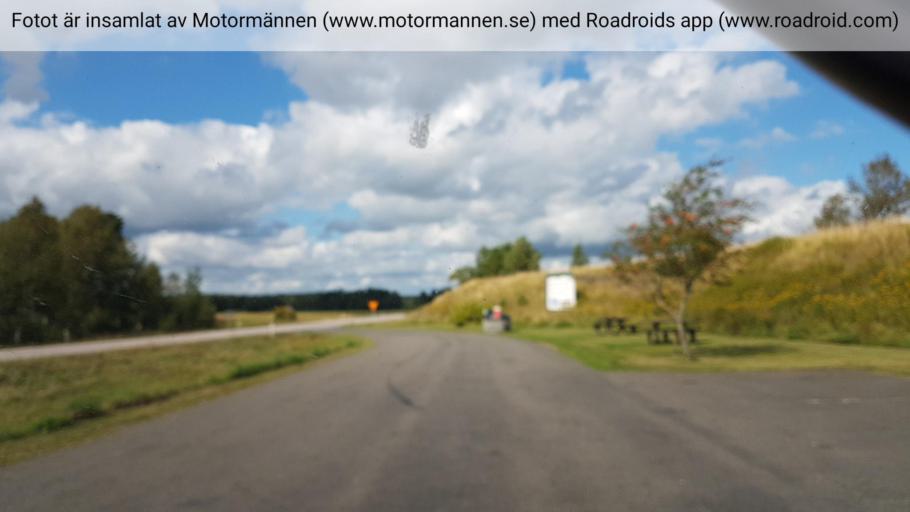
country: SE
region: Vaestra Goetaland
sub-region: Falkopings Kommun
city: Falkoeping
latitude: 57.9933
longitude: 13.5488
